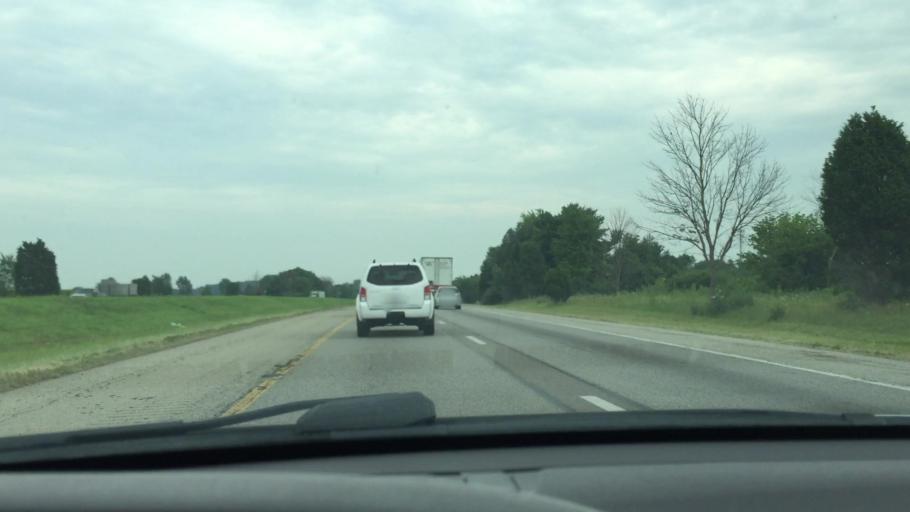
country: US
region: Ohio
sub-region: Warren County
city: Waynesville
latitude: 39.4371
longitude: -84.0641
